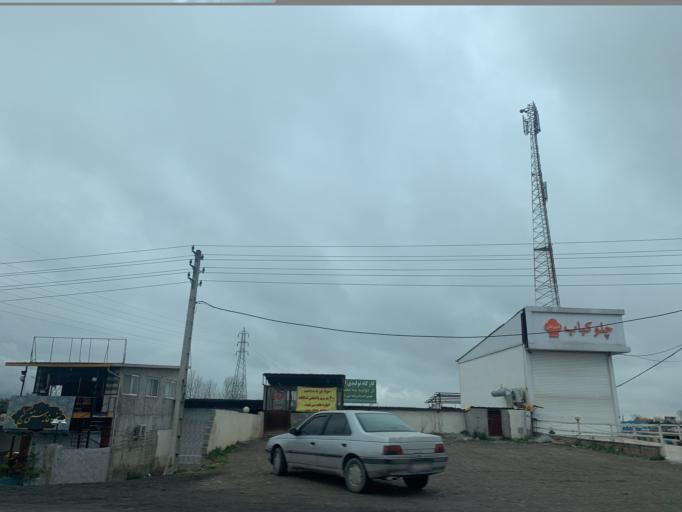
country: IR
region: Mazandaran
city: Amol
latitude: 36.4226
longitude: 52.3497
